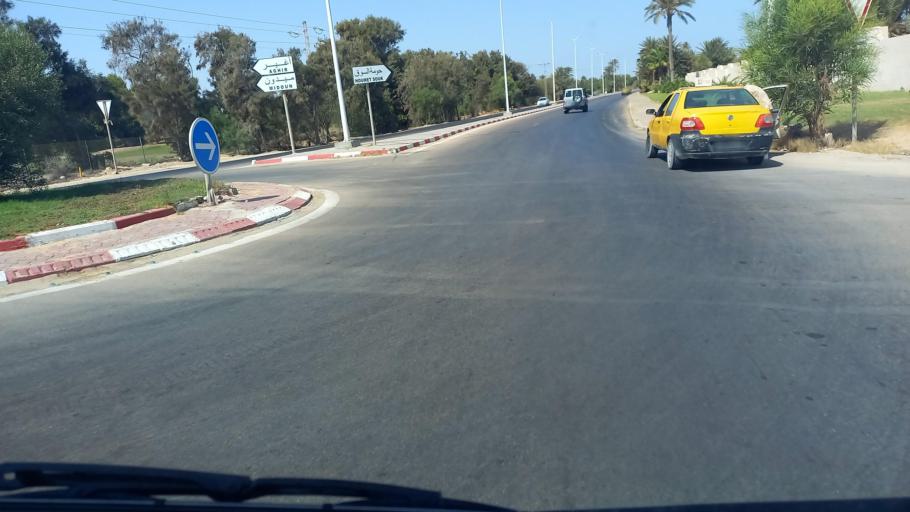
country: TN
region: Madanin
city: Midoun
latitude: 33.8252
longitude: 11.0221
